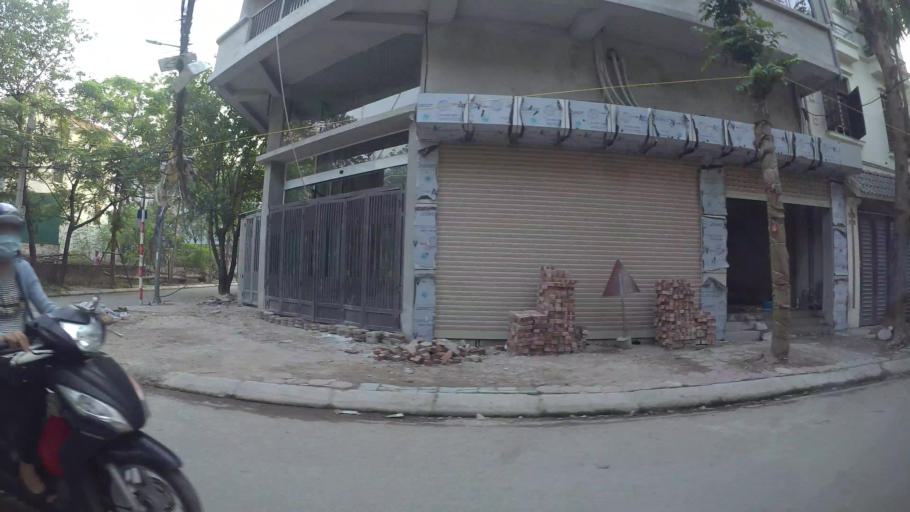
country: VN
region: Ha Noi
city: Tay Ho
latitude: 21.0686
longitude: 105.7883
